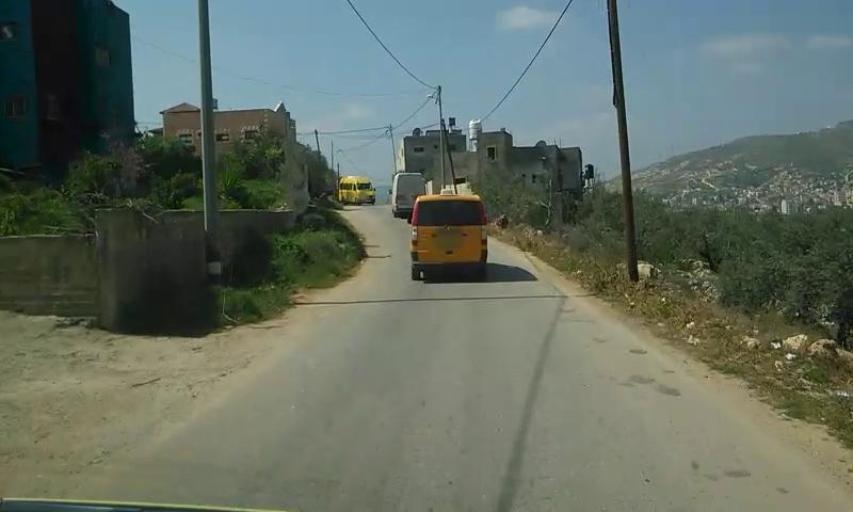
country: PS
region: West Bank
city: Udalah
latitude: 32.1431
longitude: 35.2750
